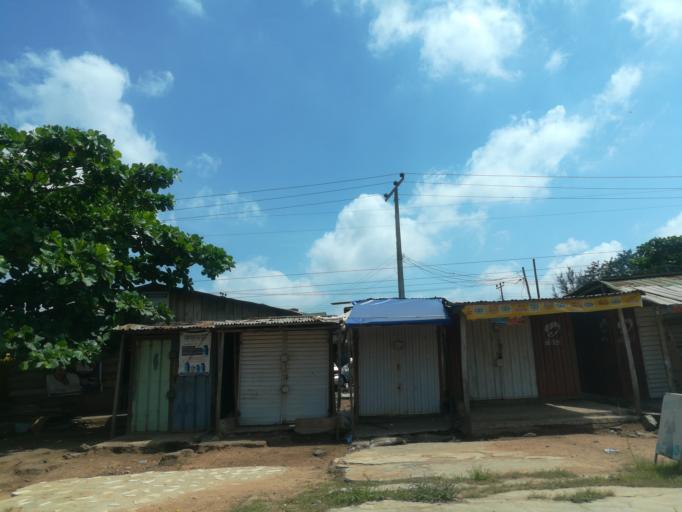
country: NG
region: Oyo
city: Ibadan
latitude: 7.3520
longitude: 3.8630
